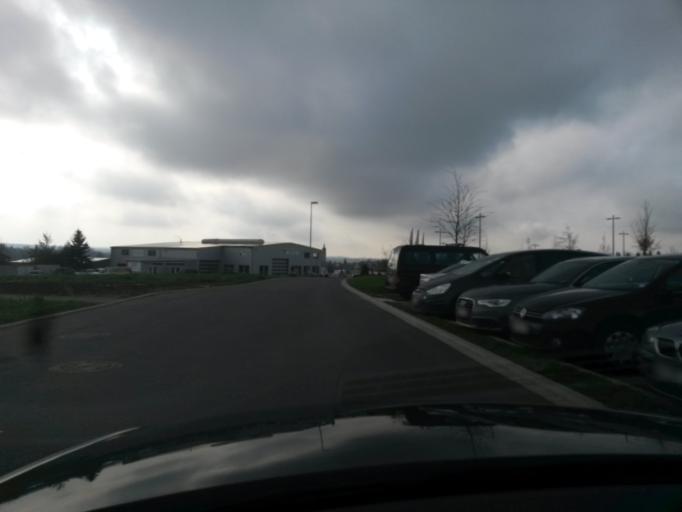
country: DE
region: Bavaria
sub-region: Regierungsbezirk Unterfranken
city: Estenfeld
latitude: 49.8383
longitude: 10.0100
